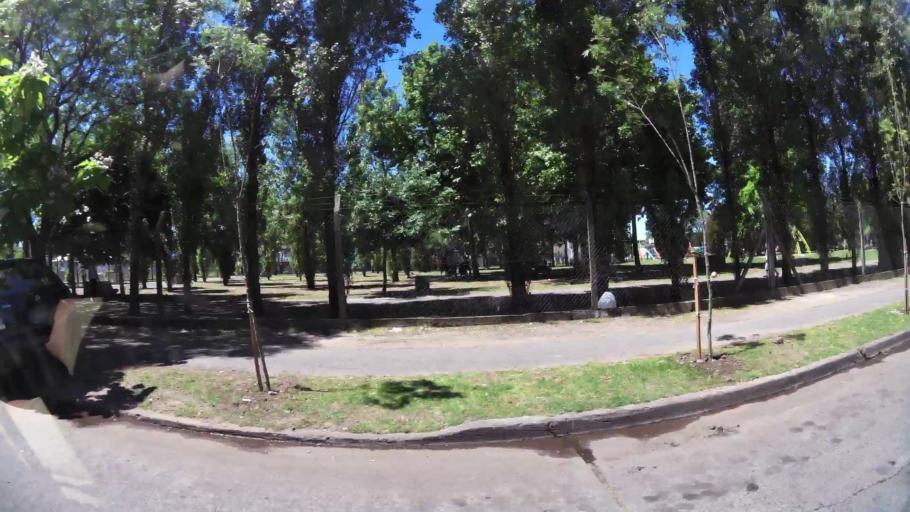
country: AR
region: Buenos Aires
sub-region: Partido de General San Martin
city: General San Martin
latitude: -34.5222
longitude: -58.5493
